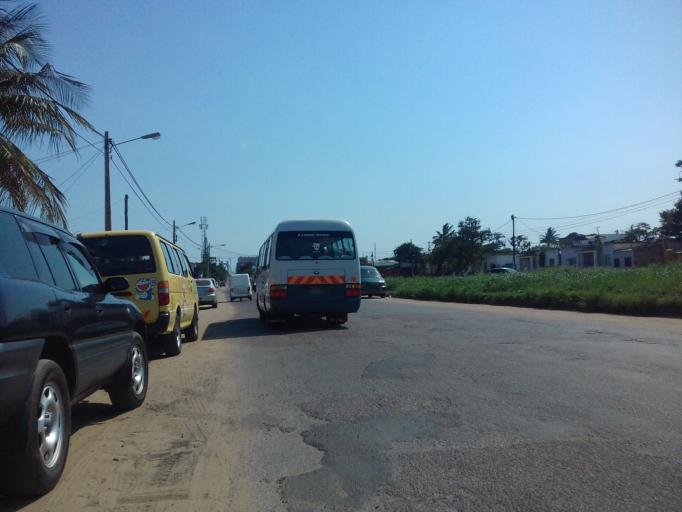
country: MZ
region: Maputo City
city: Maputo
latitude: -25.9481
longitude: 32.5708
